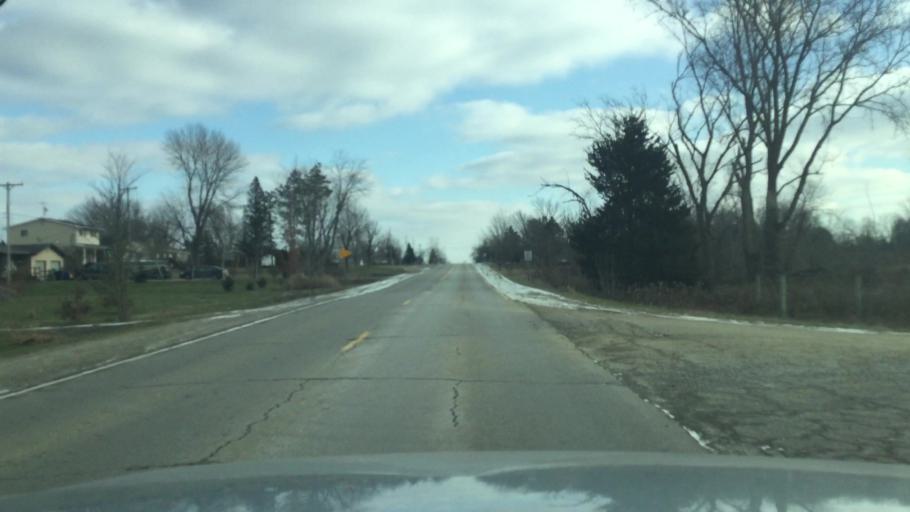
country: US
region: Michigan
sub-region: Genesee County
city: Linden
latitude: 42.8629
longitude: -83.7591
